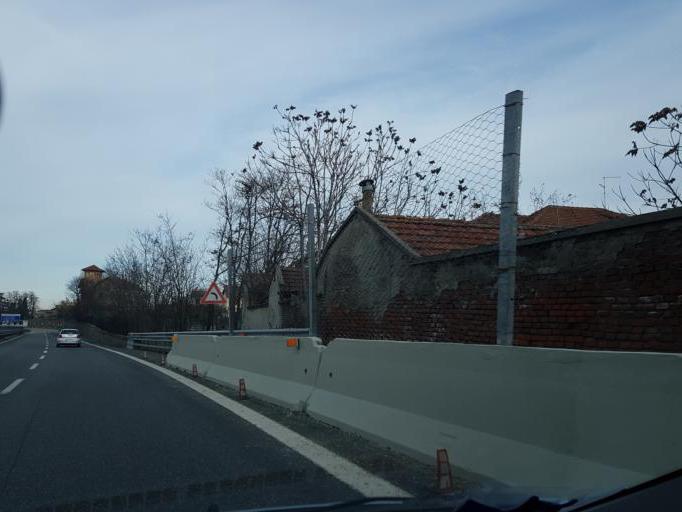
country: IT
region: Piedmont
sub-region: Provincia di Alessandria
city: Serravalle Scrivia
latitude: 44.7217
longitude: 8.8631
